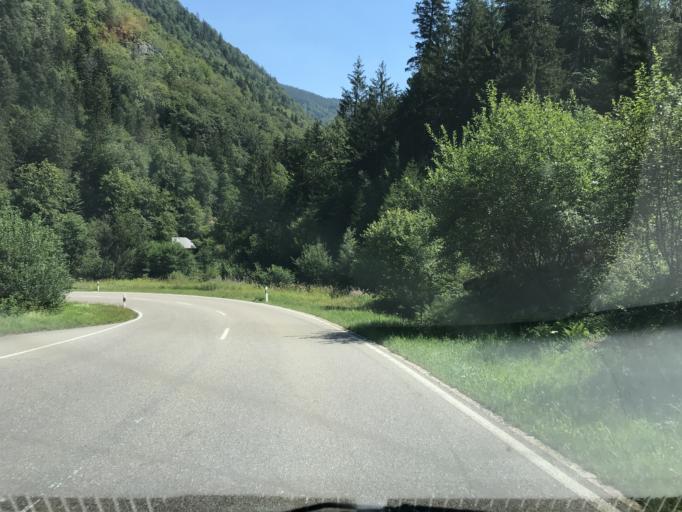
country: DE
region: Baden-Wuerttemberg
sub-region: Freiburg Region
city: Oberried
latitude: 47.9024
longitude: 7.9305
